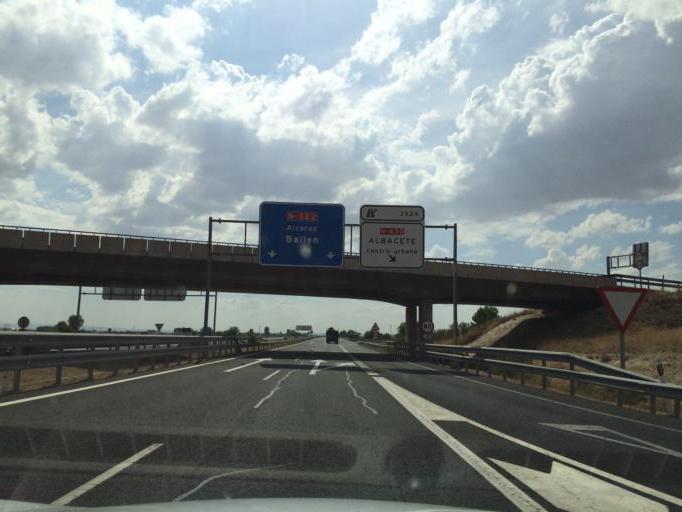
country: ES
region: Castille-La Mancha
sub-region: Provincia de Albacete
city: Albacete
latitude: 39.0022
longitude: -1.9024
